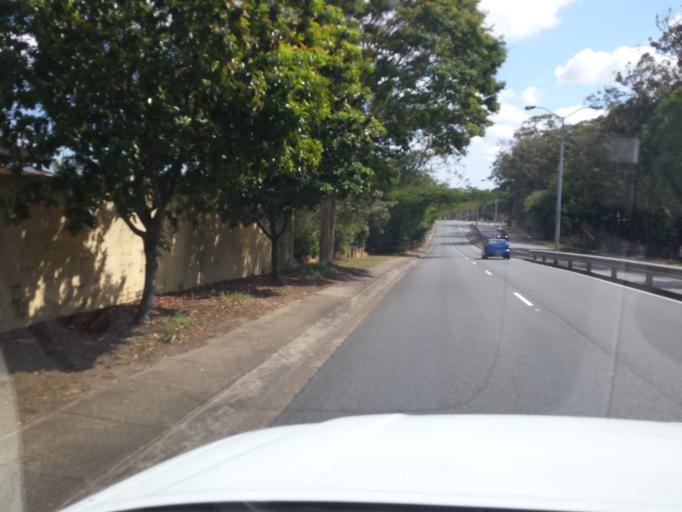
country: AU
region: Queensland
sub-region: Brisbane
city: Chermside West
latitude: -27.3902
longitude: 153.0208
